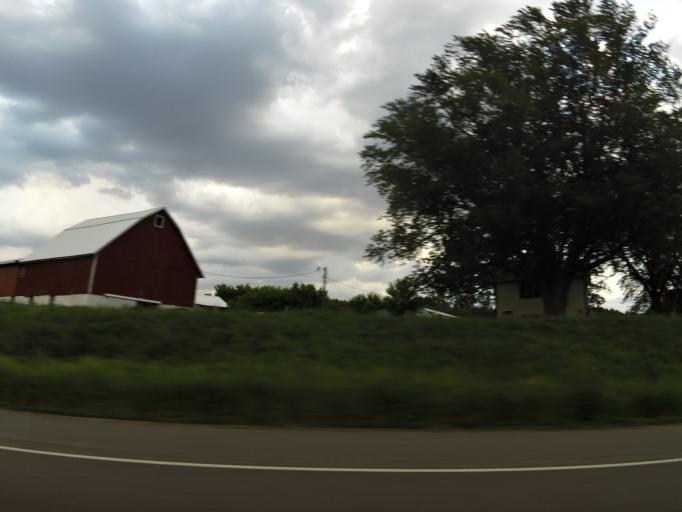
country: US
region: Wisconsin
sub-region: Eau Claire County
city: Fall Creek
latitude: 44.6833
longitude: -91.3295
